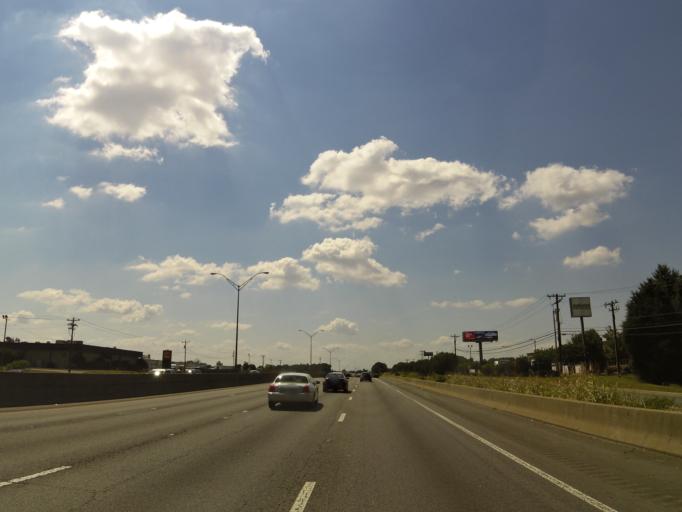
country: US
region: North Carolina
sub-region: Mecklenburg County
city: Charlotte
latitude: 35.2758
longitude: -80.8202
